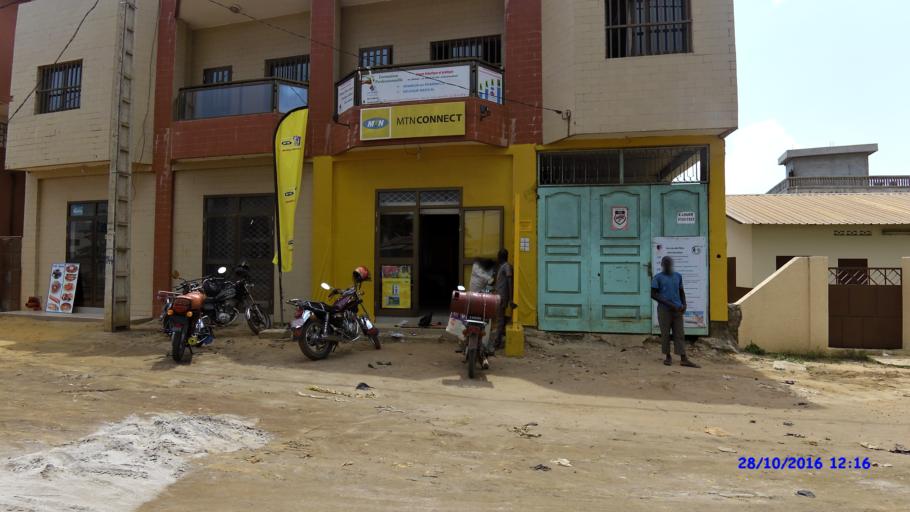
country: BJ
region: Atlantique
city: Hevie
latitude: 6.3873
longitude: 2.2963
